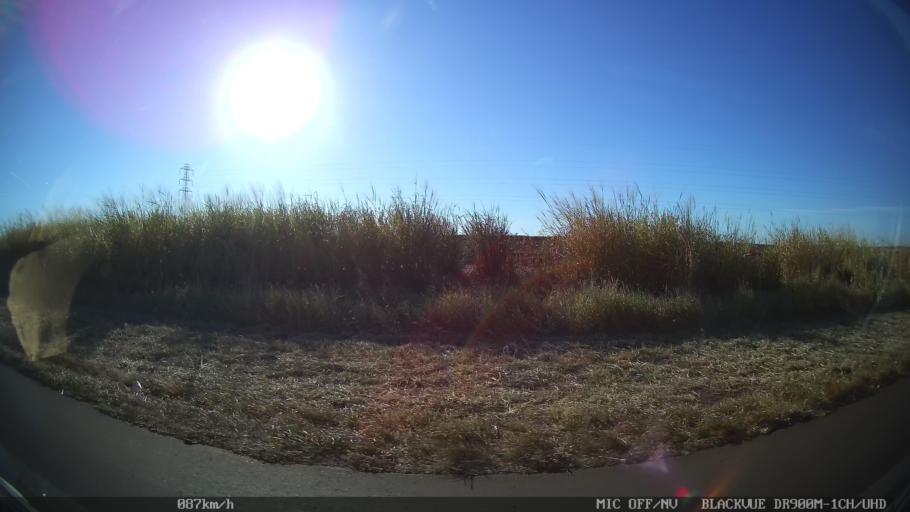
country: BR
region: Sao Paulo
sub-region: Olimpia
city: Olimpia
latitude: -20.6979
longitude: -48.9330
